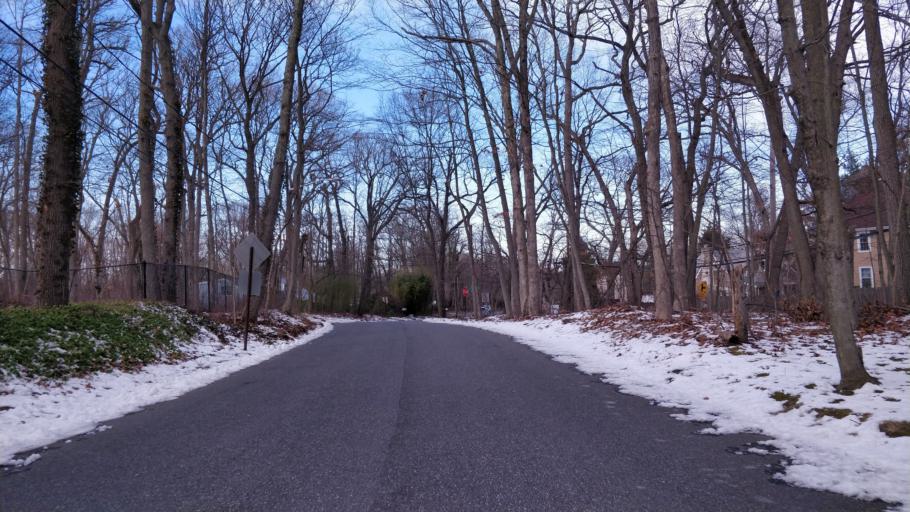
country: US
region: New York
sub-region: Suffolk County
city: Northport
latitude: 40.8869
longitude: -73.3439
